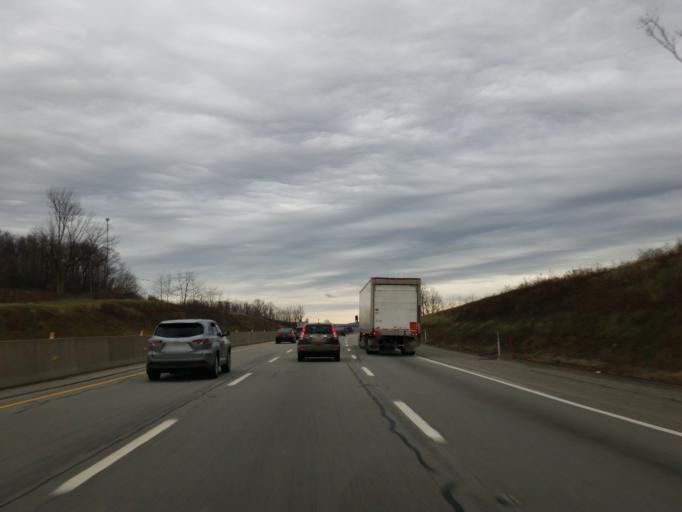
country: US
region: Pennsylvania
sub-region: Fayette County
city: Bear Rocks
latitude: 40.1111
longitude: -79.3627
